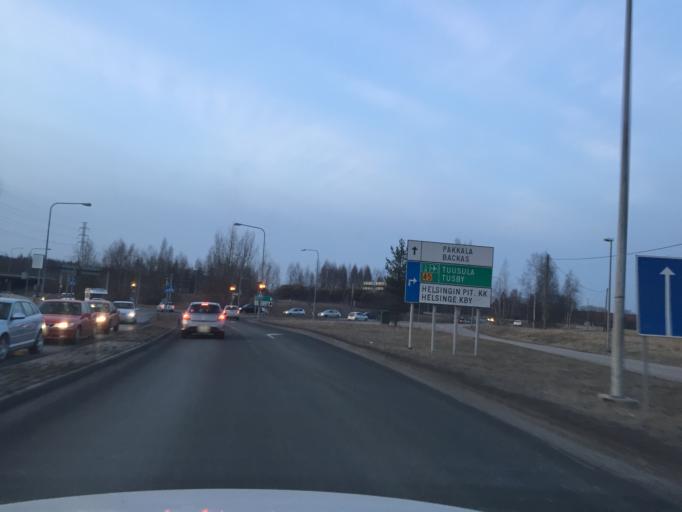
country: FI
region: Uusimaa
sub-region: Helsinki
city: Vantaa
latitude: 60.2662
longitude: 24.9731
